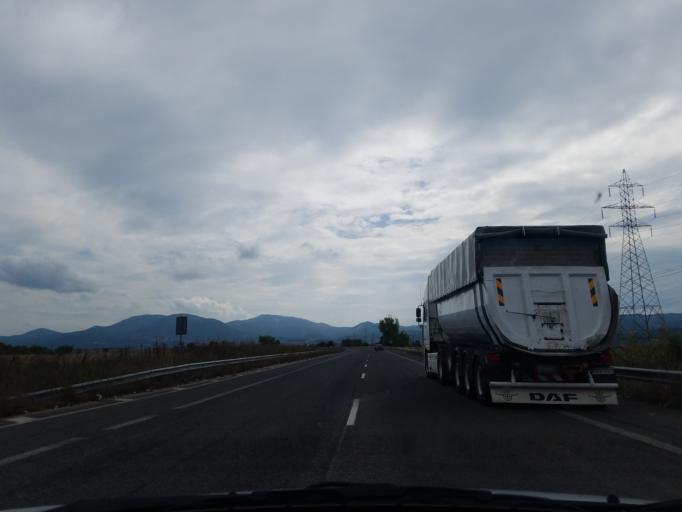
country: GR
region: Central Greece
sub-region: Nomos Fthiotidos
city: Omvriaki
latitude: 39.0603
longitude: 22.3315
